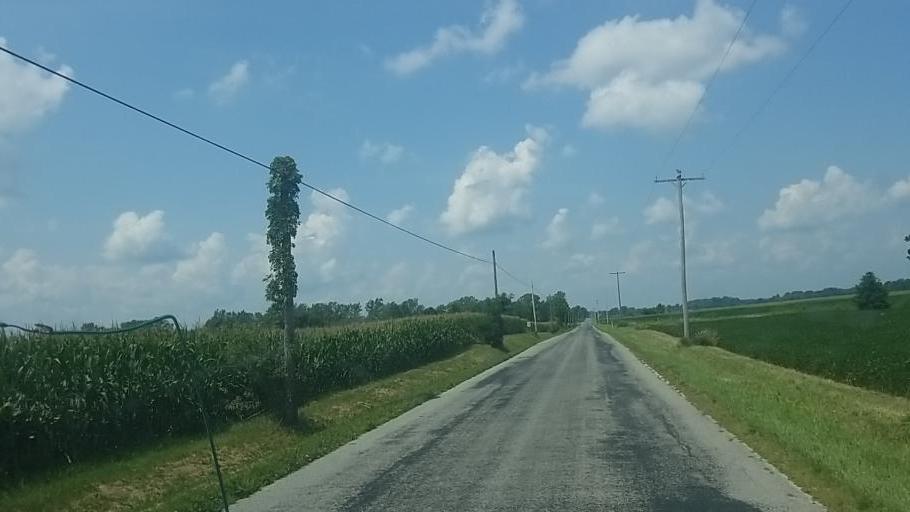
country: US
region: Ohio
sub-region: Crawford County
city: Crestline
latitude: 40.7988
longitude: -82.7106
